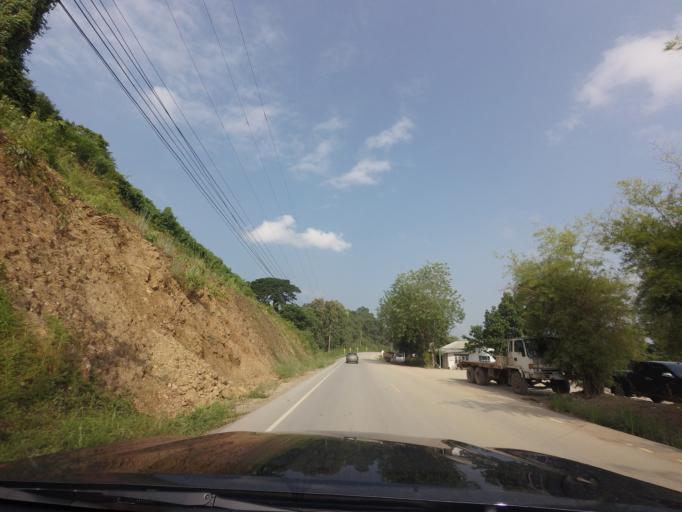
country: TH
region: Loei
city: Chiang Khan
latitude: 17.8484
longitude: 101.5850
